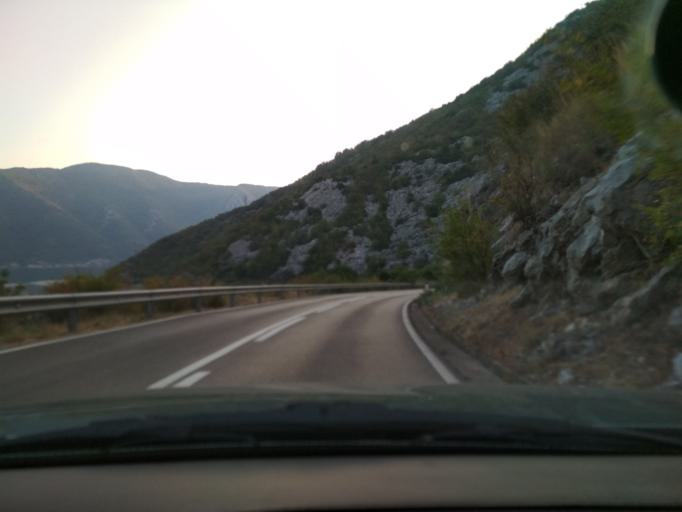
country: ME
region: Kotor
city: Risan
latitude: 42.5118
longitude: 18.6810
